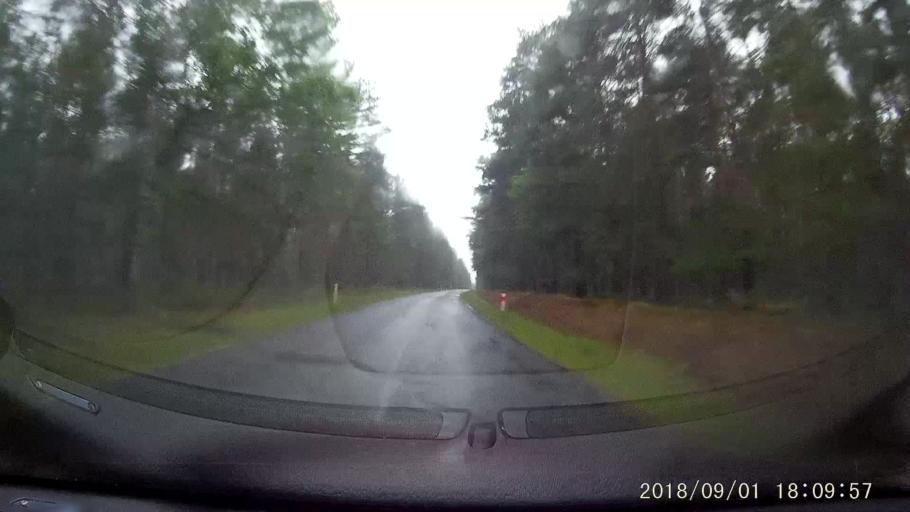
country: PL
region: Lubusz
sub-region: Powiat zaganski
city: Gozdnica
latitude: 51.3389
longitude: 15.1002
